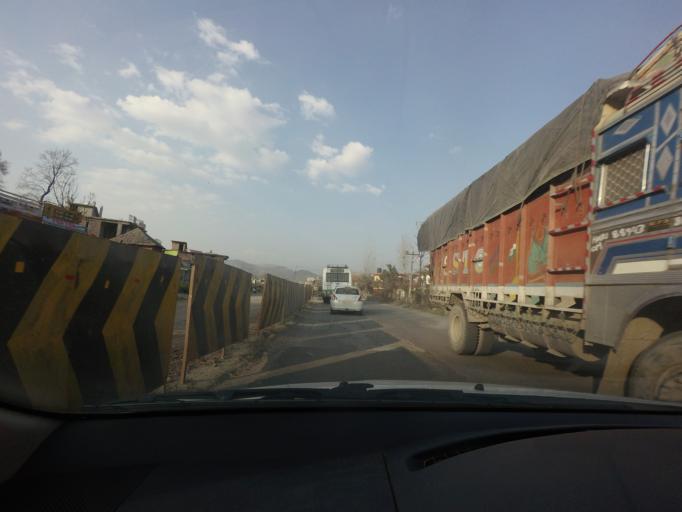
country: IN
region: Himachal Pradesh
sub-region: Mandi
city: Sundarnagar
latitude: 31.5902
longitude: 76.9233
